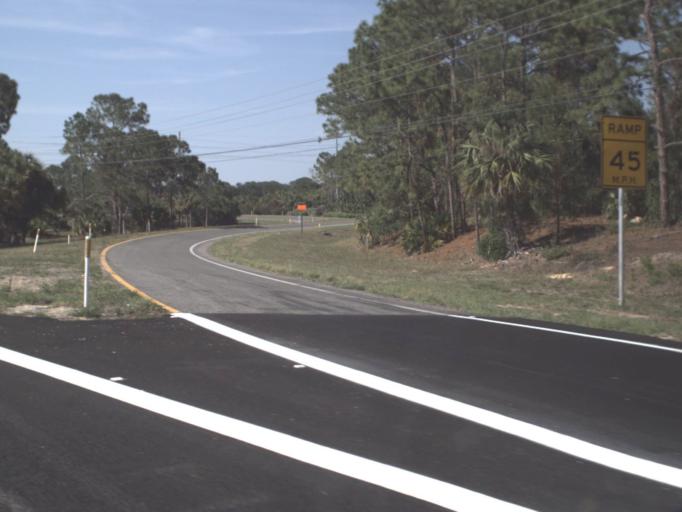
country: US
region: Florida
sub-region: Brevard County
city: Port Saint John
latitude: 28.5253
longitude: -80.7886
